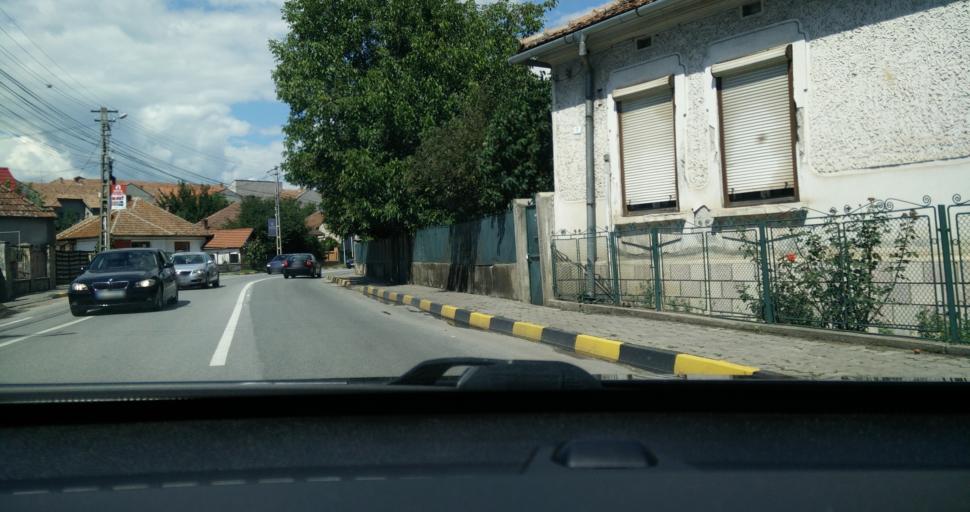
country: RO
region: Alba
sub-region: Municipiul Sebes
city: Sebes
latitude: 45.9558
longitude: 23.5658
